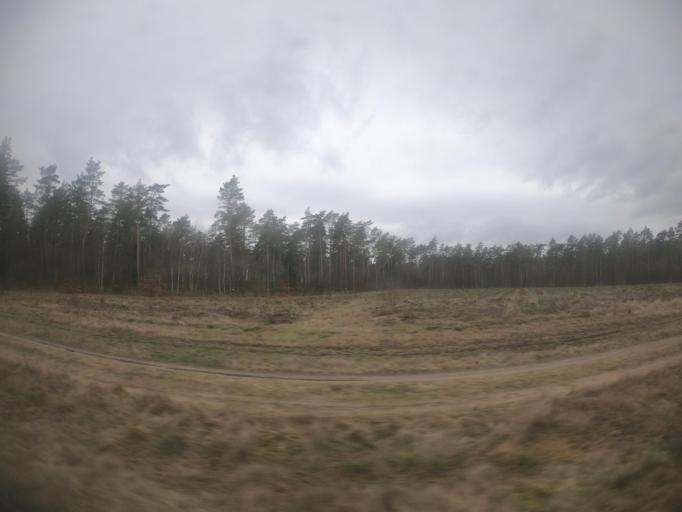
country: PL
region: West Pomeranian Voivodeship
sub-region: Powiat szczecinecki
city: Bialy Bor
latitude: 53.8184
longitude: 16.8693
